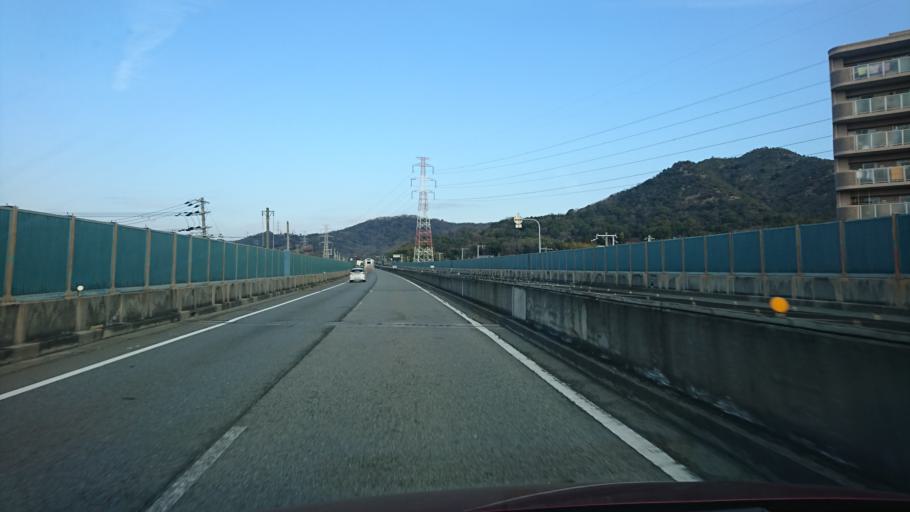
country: JP
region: Hyogo
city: Himeji
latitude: 34.8409
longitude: 134.7375
